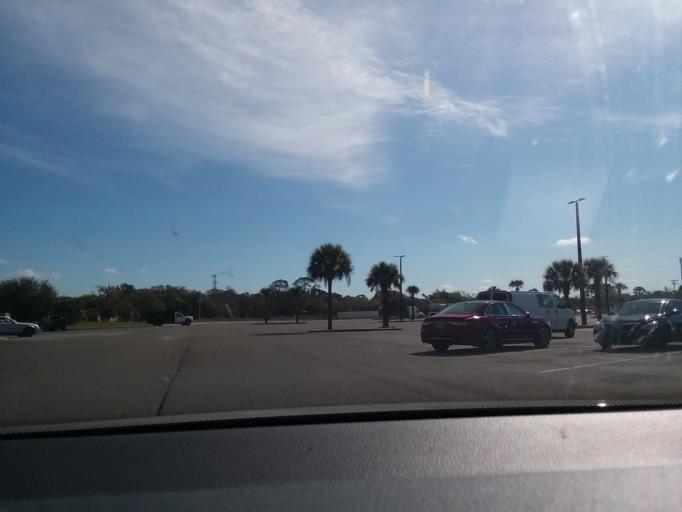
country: US
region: Florida
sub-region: Duval County
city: Jacksonville
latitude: 30.3771
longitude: -81.6544
